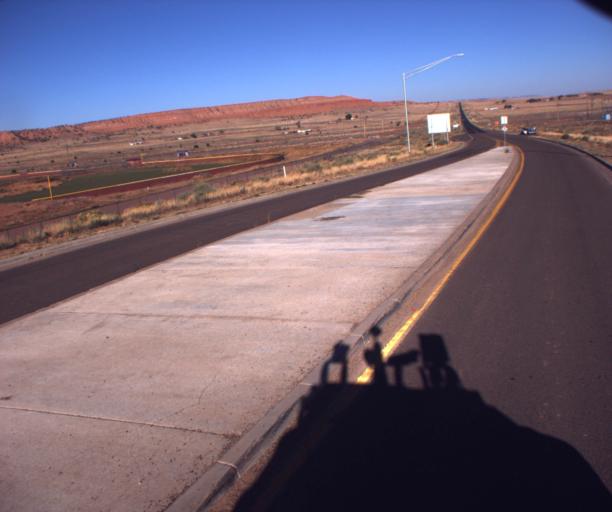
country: US
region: Arizona
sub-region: Apache County
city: Ganado
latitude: 35.7552
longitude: -109.6277
